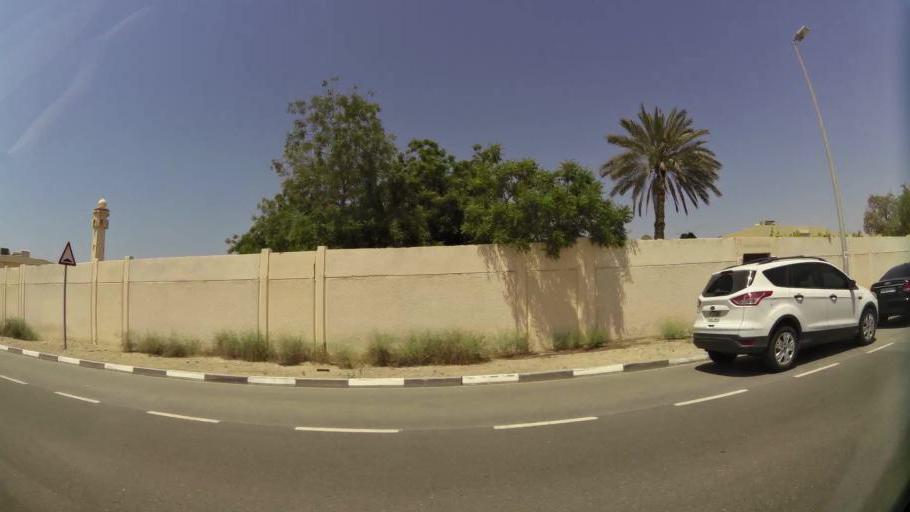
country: AE
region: Ash Shariqah
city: Sharjah
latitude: 25.2941
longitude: 55.3449
